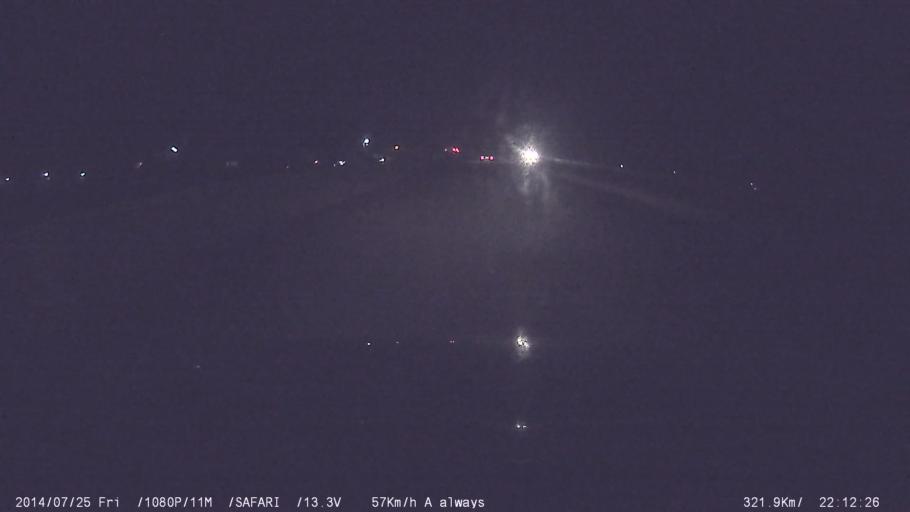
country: IN
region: Tamil Nadu
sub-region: Tiruppur
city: Avinashi
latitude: 11.1553
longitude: 77.2144
